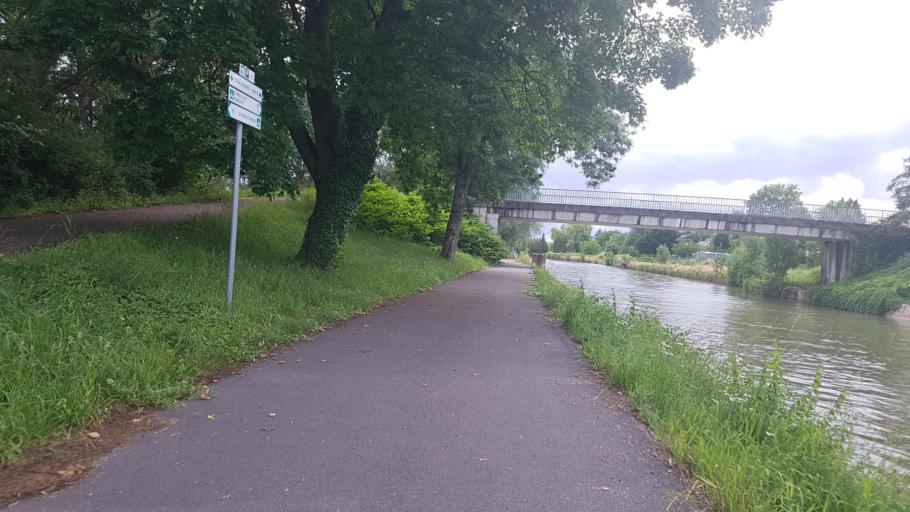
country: FR
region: Lorraine
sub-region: Departement de la Moselle
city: Dieuze
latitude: 48.6902
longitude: 6.7046
